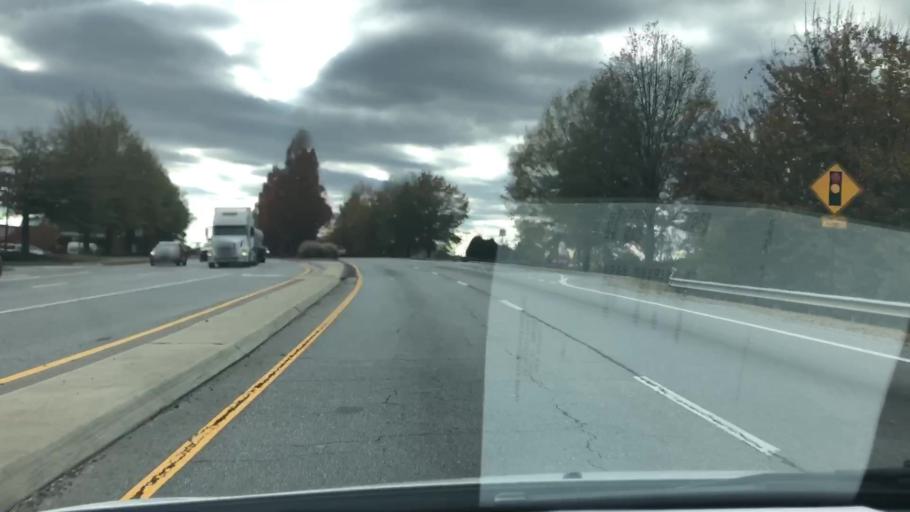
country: US
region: Georgia
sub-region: Fulton County
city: Johns Creek
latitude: 34.0747
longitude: -84.1651
